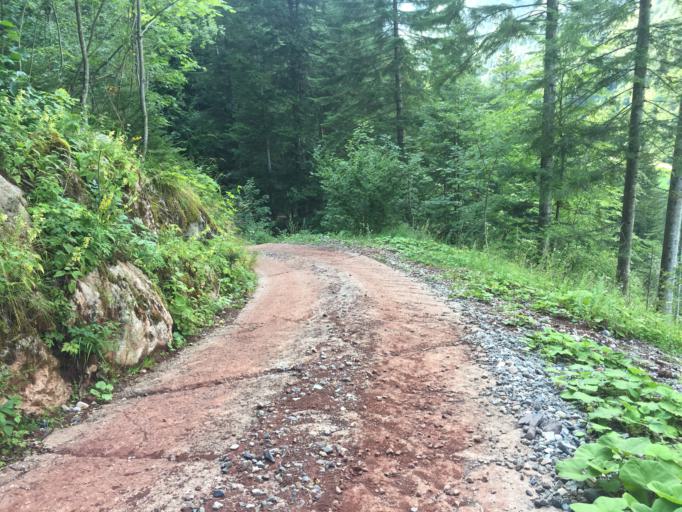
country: IT
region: Friuli Venezia Giulia
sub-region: Provincia di Udine
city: Forni Avoltri
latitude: 46.5735
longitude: 12.7909
